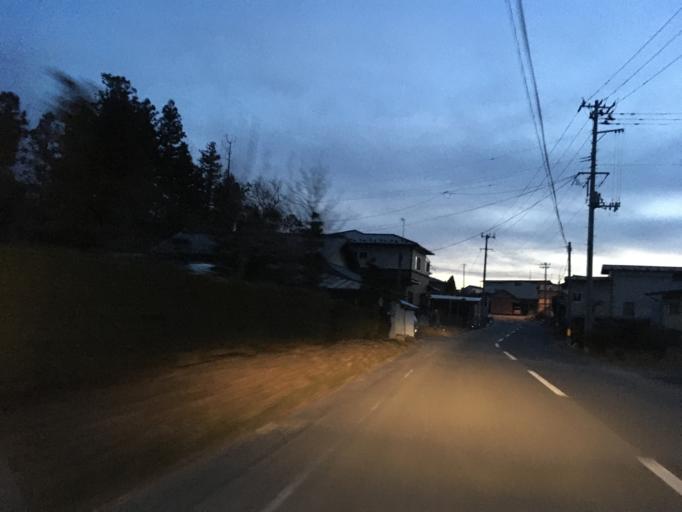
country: JP
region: Miyagi
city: Wakuya
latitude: 38.7140
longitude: 141.1466
